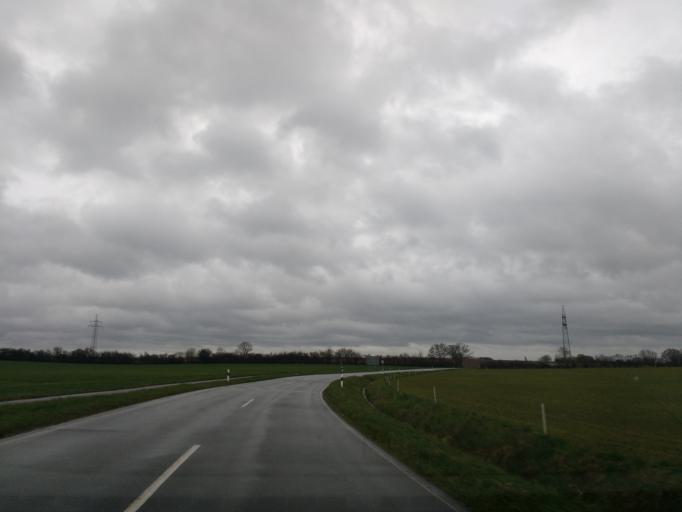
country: DE
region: Schleswig-Holstein
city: Blekendorf
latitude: 54.2945
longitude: 10.6788
